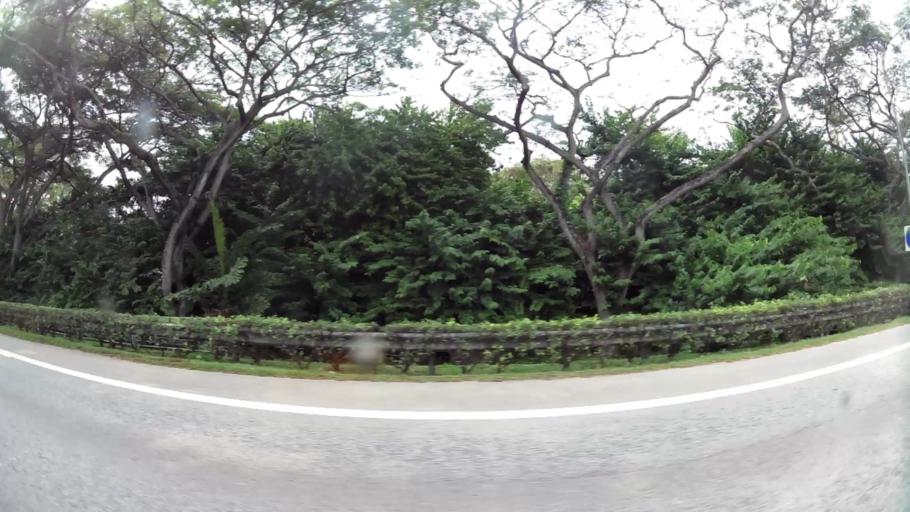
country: SG
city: Singapore
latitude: 1.3290
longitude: 103.9746
